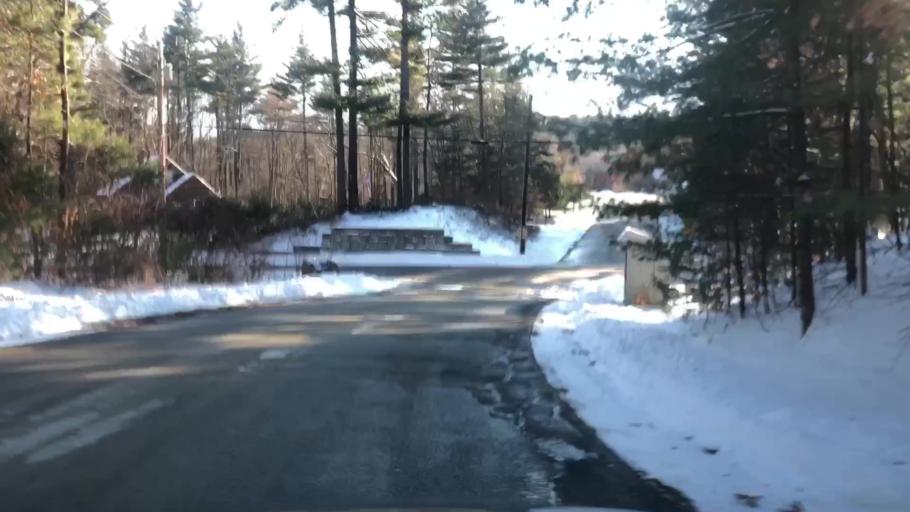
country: US
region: New Hampshire
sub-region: Hillsborough County
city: Wilton
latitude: 42.8132
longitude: -71.7146
